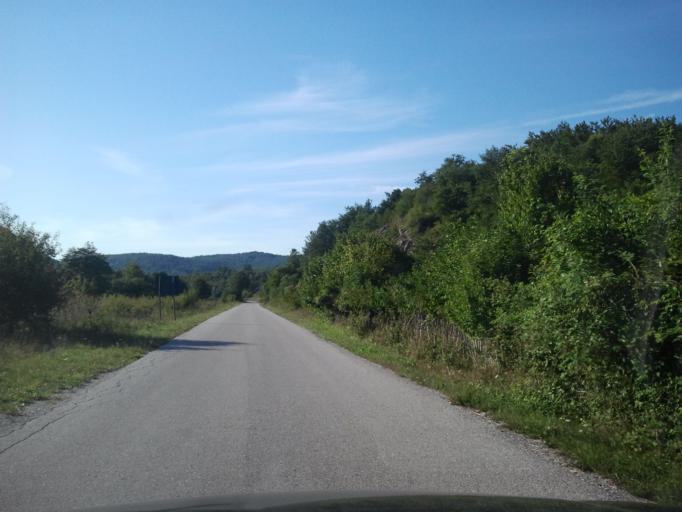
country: HR
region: Zadarska
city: Obrovac
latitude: 44.3402
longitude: 15.6439
